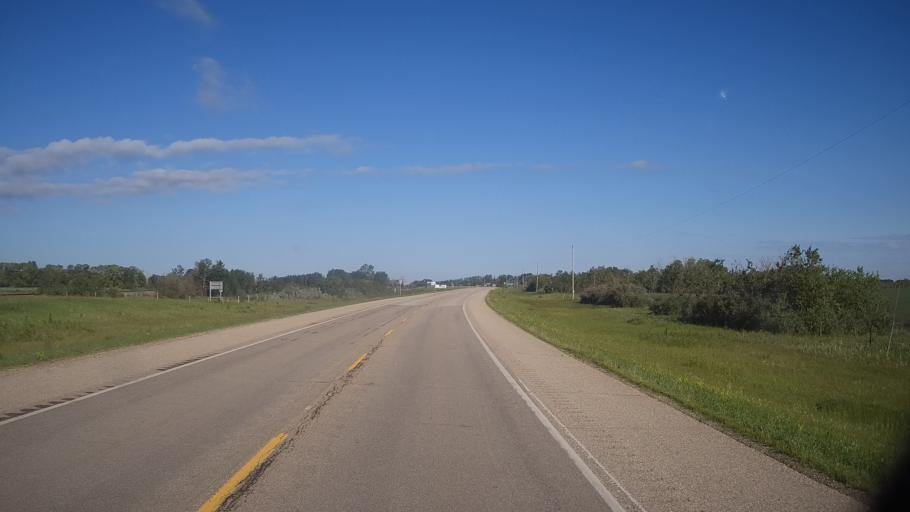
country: CA
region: Saskatchewan
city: Lanigan
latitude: 51.8719
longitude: -105.1753
